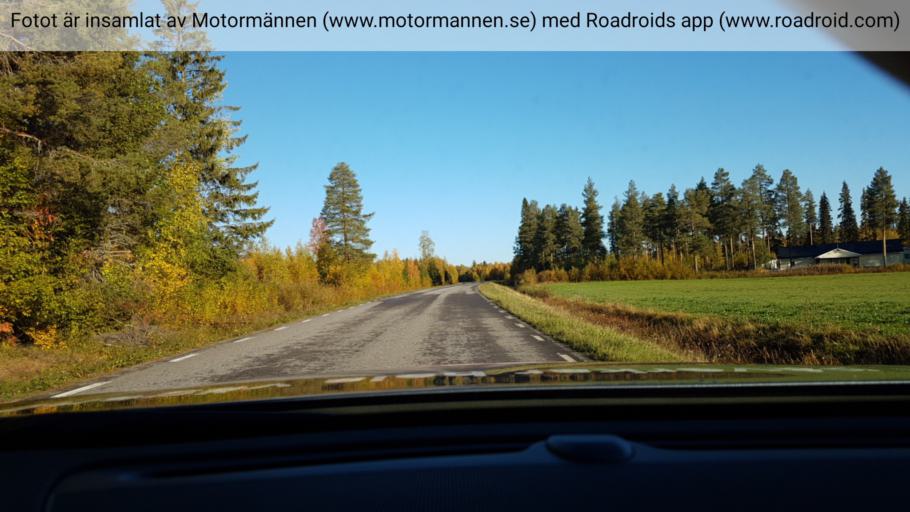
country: SE
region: Norrbotten
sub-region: Bodens Kommun
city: Boden
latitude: 65.9029
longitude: 21.6690
